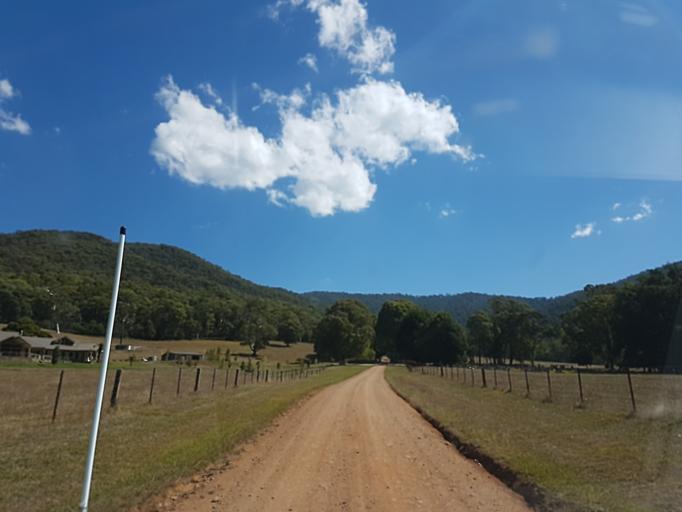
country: AU
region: Victoria
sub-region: Alpine
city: Mount Beauty
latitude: -36.8729
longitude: 147.0595
